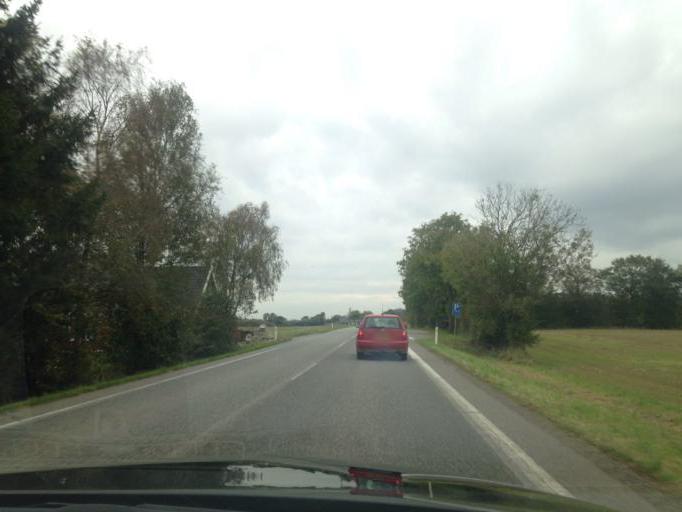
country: DK
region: South Denmark
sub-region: Kolding Kommune
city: Christiansfeld
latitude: 55.4237
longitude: 9.4763
